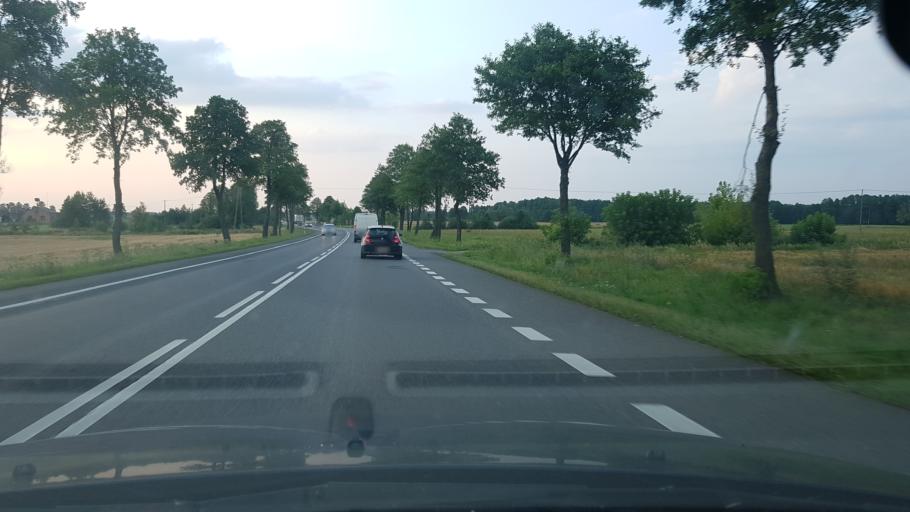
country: PL
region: Masovian Voivodeship
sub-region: Powiat mlawski
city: Strzegowo
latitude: 52.9281
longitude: 20.2861
